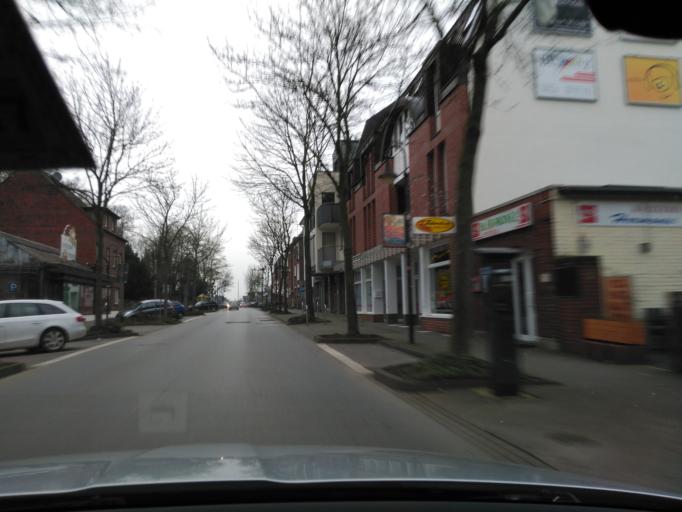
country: DE
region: North Rhine-Westphalia
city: Wegberg
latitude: 51.1429
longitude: 6.2788
